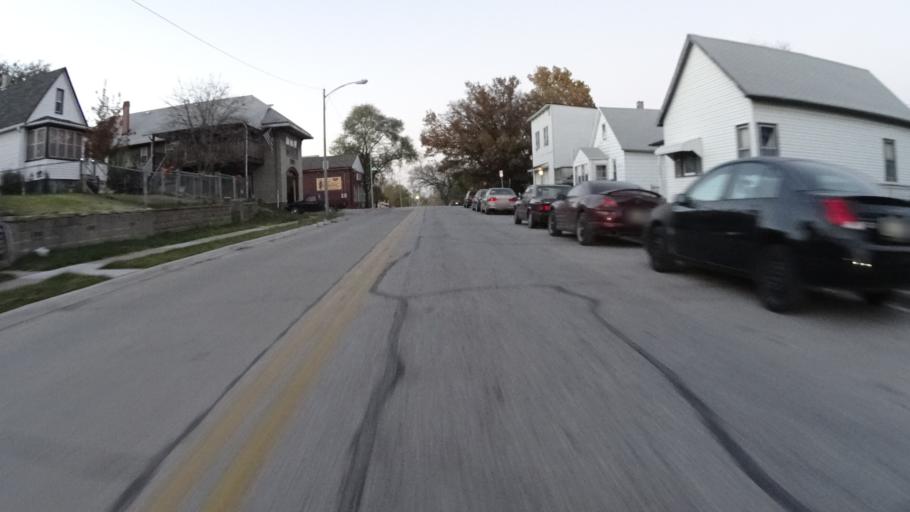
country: US
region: Nebraska
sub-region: Douglas County
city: Omaha
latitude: 41.2129
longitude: -95.9626
